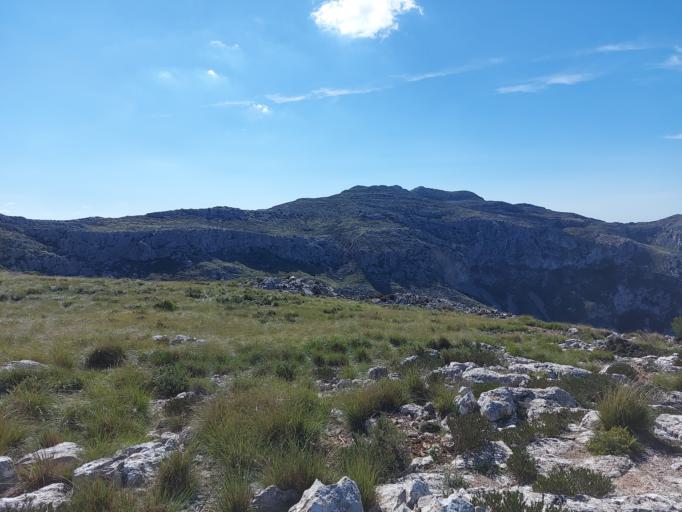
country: ES
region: Balearic Islands
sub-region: Illes Balears
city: Deia
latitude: 39.7503
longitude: 2.6670
